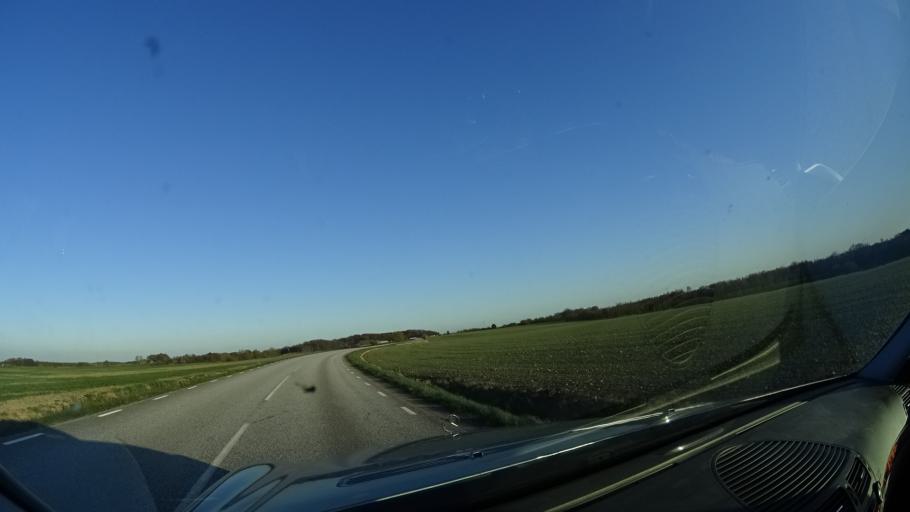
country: SE
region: Skane
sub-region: Klippans Kommun
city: Ljungbyhed
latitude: 55.9762
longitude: 13.2013
